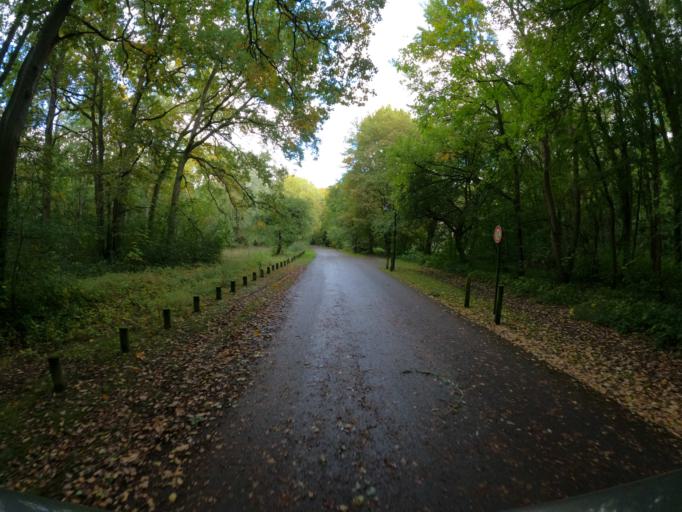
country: FR
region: Ile-de-France
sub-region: Departement de Seine-et-Marne
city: Montevrain
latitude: 48.8834
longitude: 2.7560
